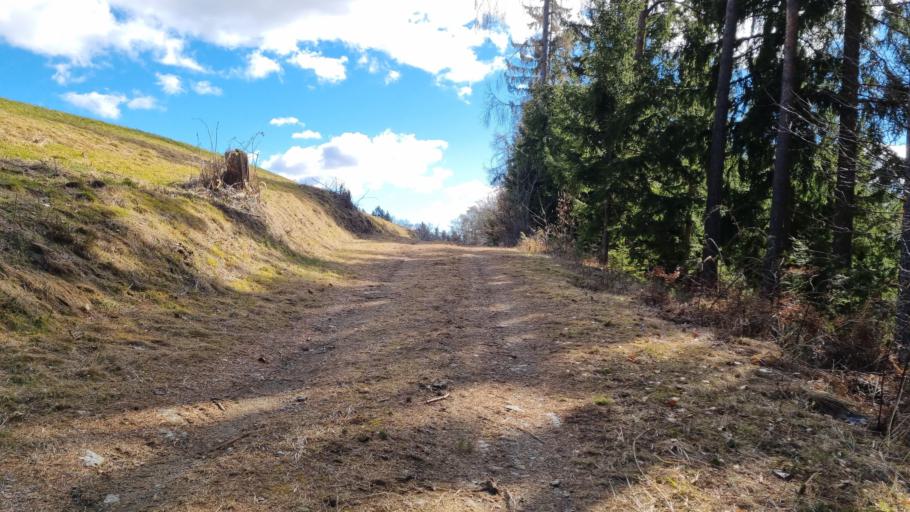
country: AT
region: Styria
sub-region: Politischer Bezirk Graz-Umgebung
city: Sankt Radegund bei Graz
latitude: 47.1606
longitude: 15.4825
